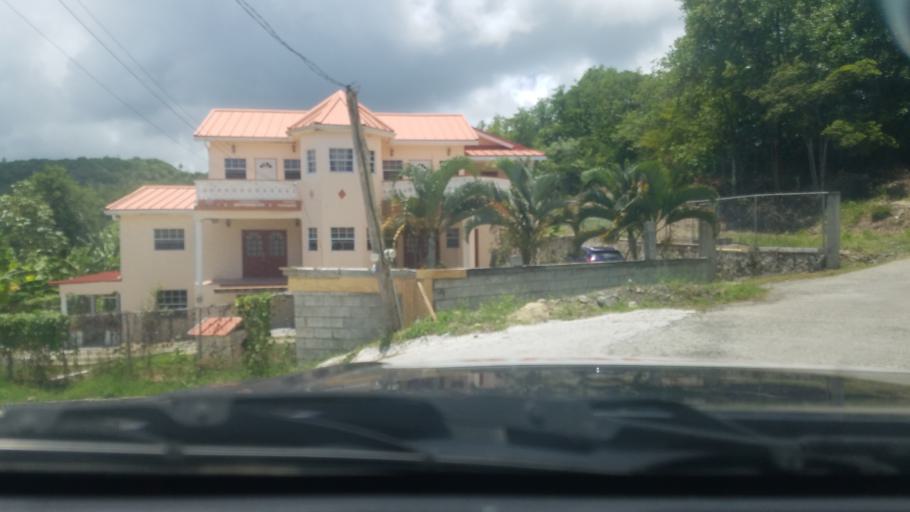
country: LC
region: Dennery Quarter
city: Dennery
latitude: 13.9189
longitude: -60.9003
